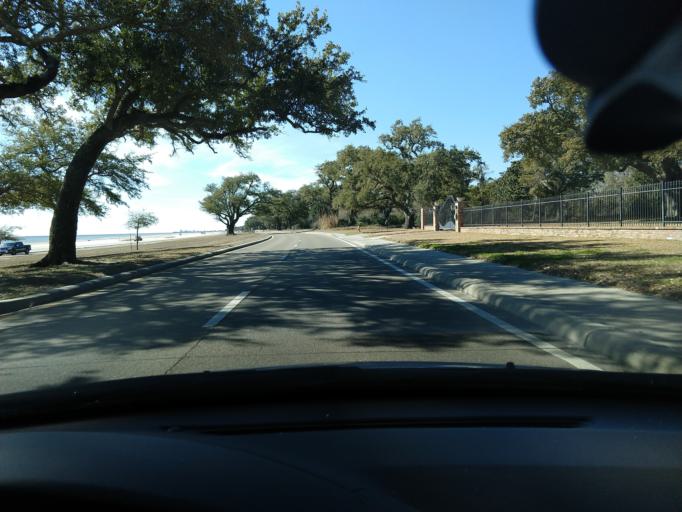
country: US
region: Mississippi
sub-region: Harrison County
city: Pass Christian
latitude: 30.3273
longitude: -89.2088
